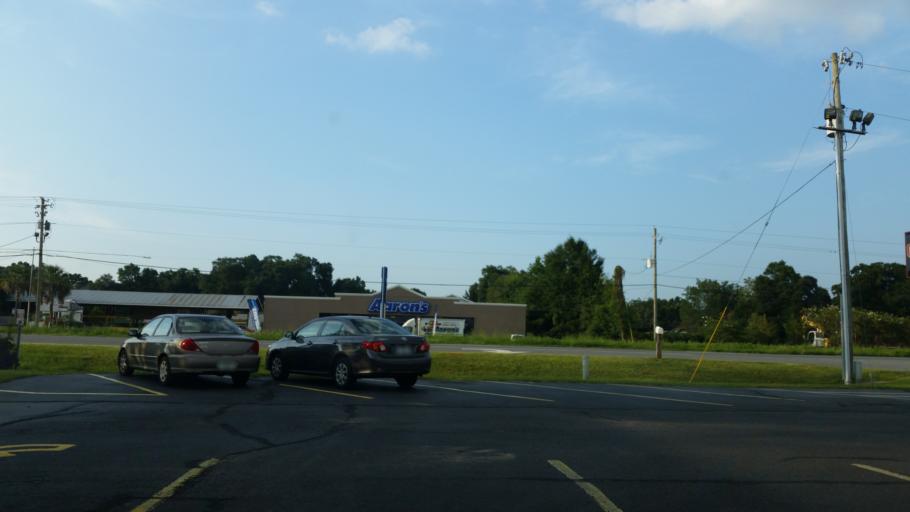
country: US
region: Florida
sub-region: Santa Rosa County
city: Pace
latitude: 30.6033
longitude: -87.1419
